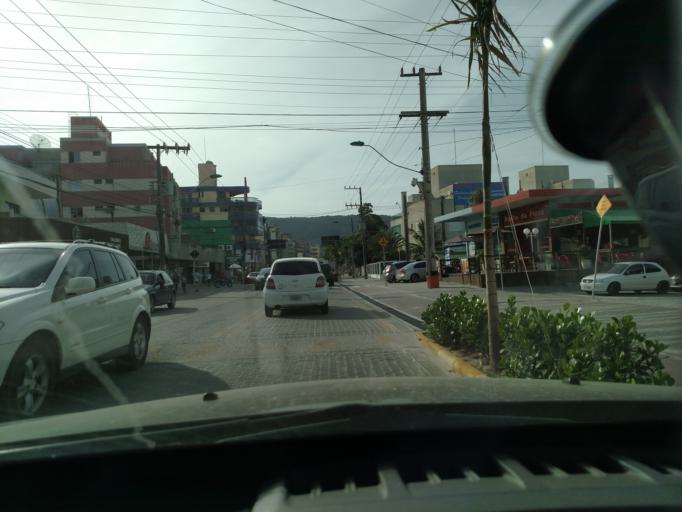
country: BR
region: Santa Catarina
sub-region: Porto Belo
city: Porto Belo
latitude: -27.1448
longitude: -48.5039
